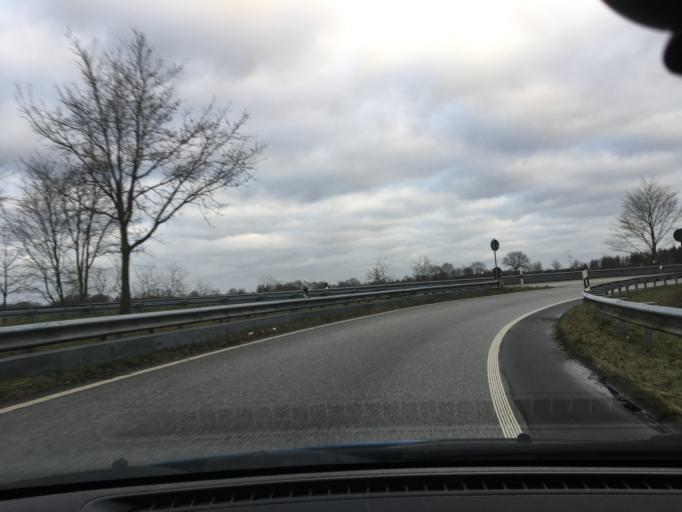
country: DE
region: Schleswig-Holstein
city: Tensbuttel-Rost
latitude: 54.1198
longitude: 9.2591
